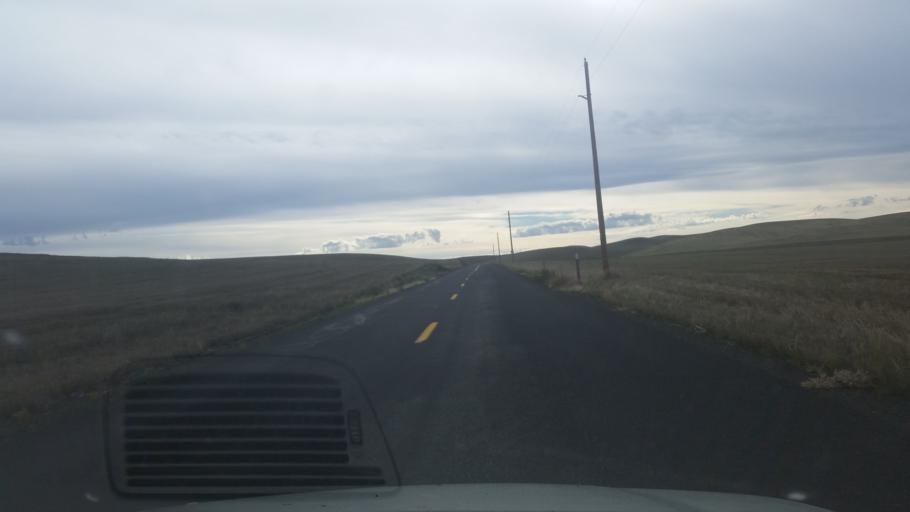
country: US
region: Washington
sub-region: Spokane County
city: Cheney
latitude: 47.3001
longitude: -117.4924
